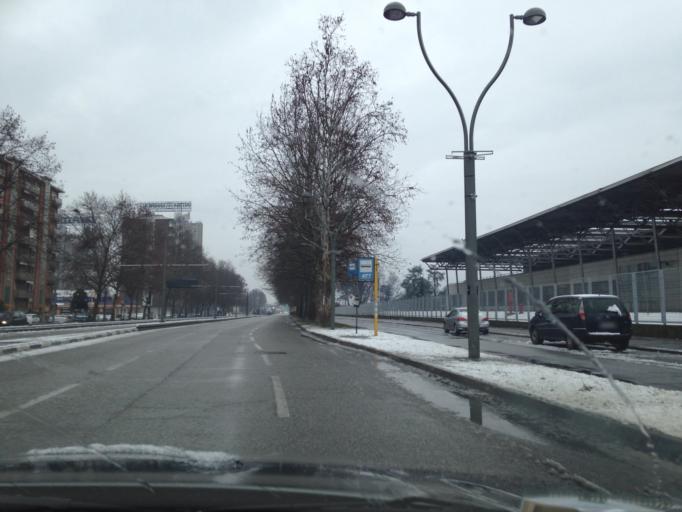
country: IT
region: Piedmont
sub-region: Provincia di Torino
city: Turin
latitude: 45.1129
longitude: 7.7074
